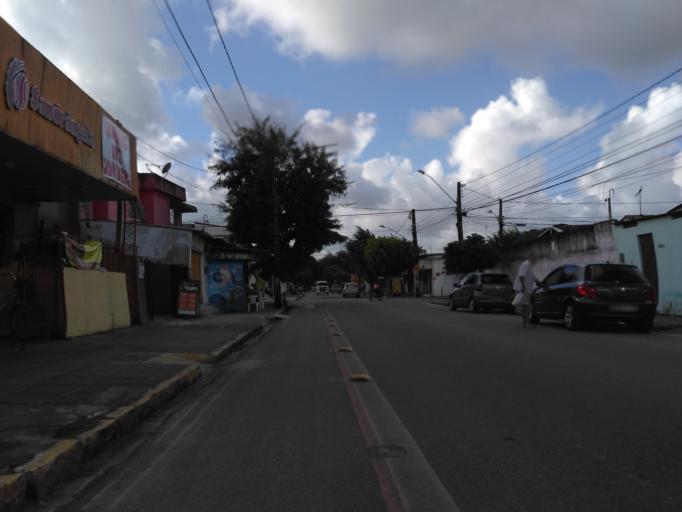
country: BR
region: Pernambuco
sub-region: Recife
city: Recife
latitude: -8.0562
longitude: -34.9419
